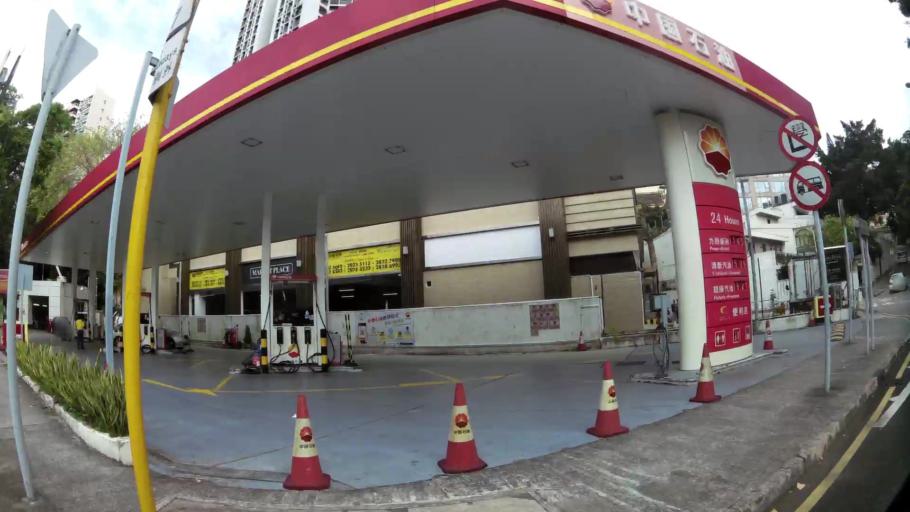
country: HK
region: Wanchai
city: Wan Chai
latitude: 22.2707
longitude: 114.1914
